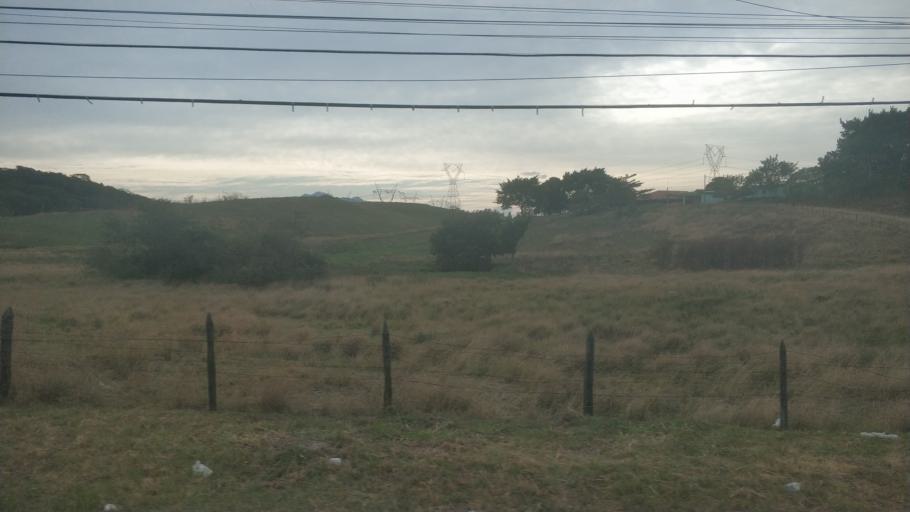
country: BR
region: Rio de Janeiro
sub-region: Seropedica
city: Seropedica
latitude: -22.7812
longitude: -43.6597
